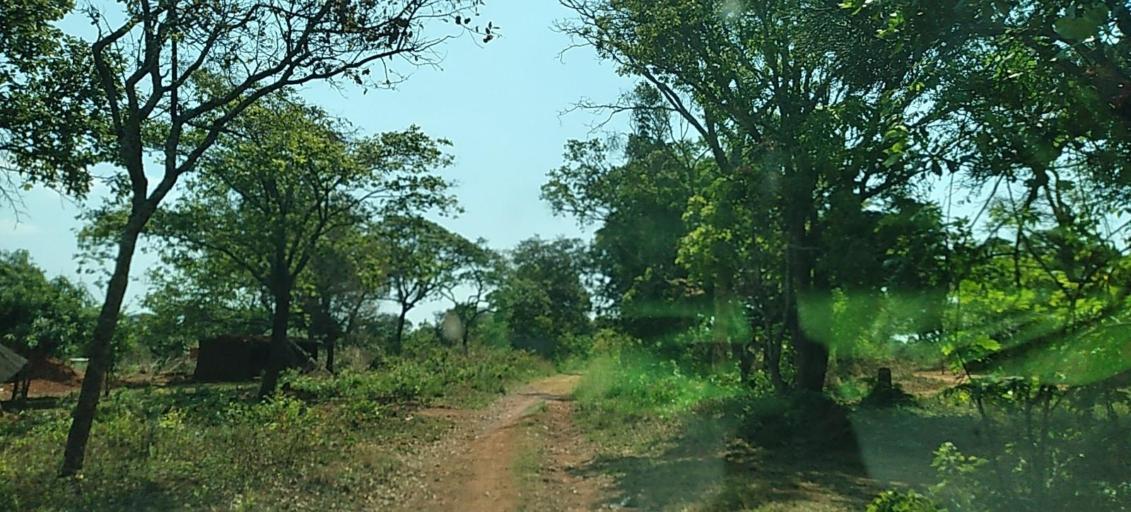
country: CD
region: Katanga
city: Kolwezi
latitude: -11.2821
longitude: 25.1438
